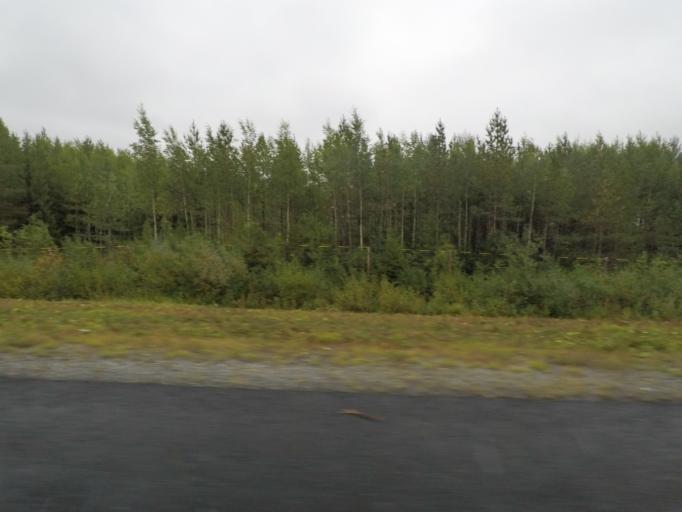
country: FI
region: Northern Savo
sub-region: Kuopio
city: Kuopio
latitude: 62.7885
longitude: 27.5941
